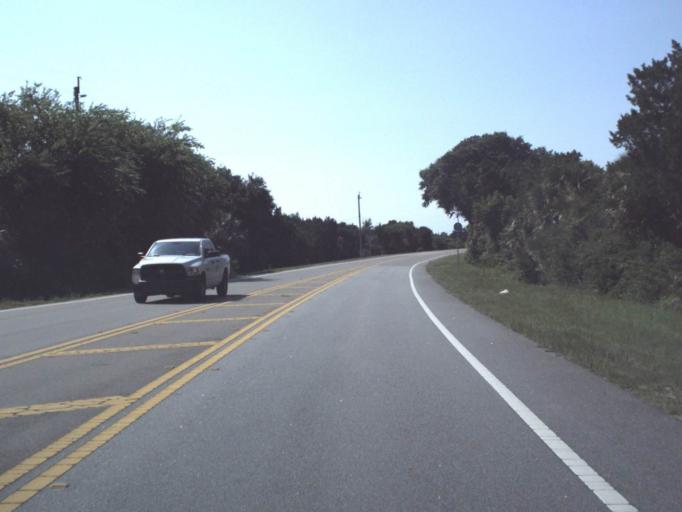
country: US
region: Florida
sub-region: Duval County
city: Atlantic Beach
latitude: 30.4578
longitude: -81.4180
